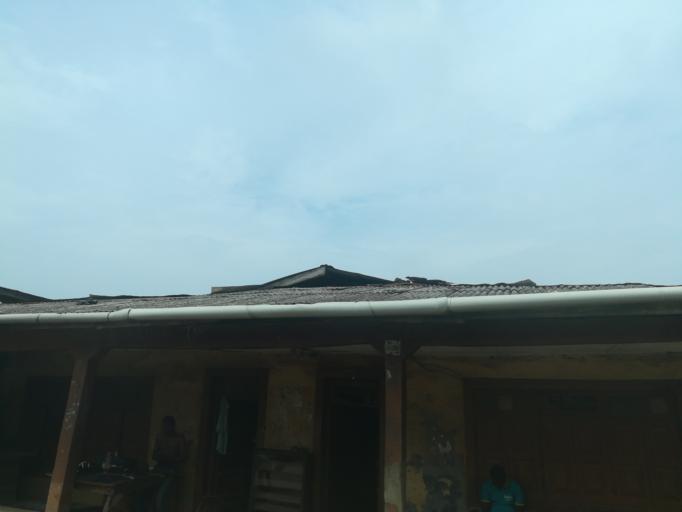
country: NG
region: Lagos
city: Ikorodu
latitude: 6.6103
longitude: 3.5045
